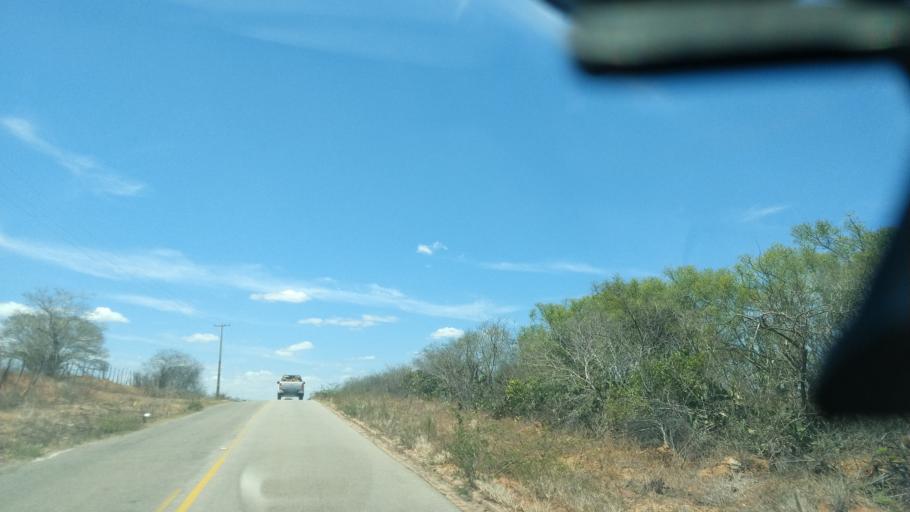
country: BR
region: Rio Grande do Norte
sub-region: Sao Paulo Do Potengi
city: Sao Paulo do Potengi
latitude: -5.9017
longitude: -35.6164
